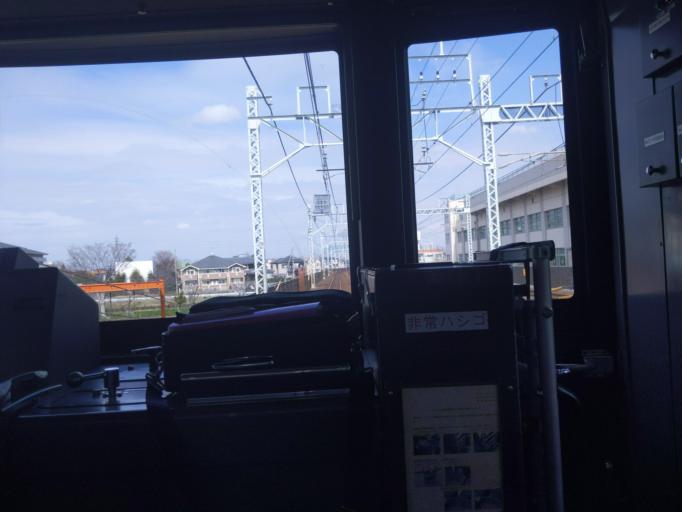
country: JP
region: Saitama
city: Soka
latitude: 35.8041
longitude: 139.7948
